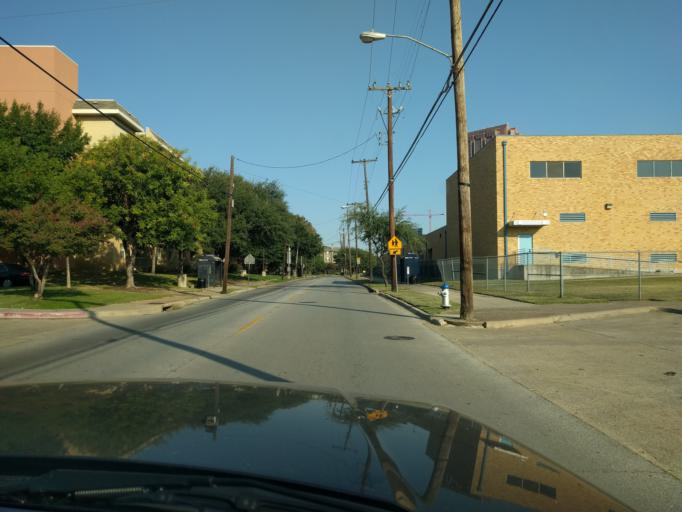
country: US
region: Texas
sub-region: Dallas County
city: Dallas
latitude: 32.8007
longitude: -96.7894
